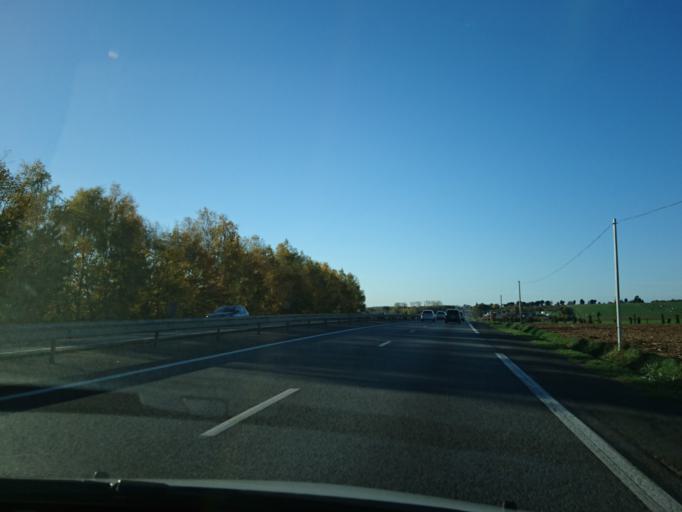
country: FR
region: Brittany
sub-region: Departement d'Ille-et-Vilaine
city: Saint-Gilles
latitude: 48.1622
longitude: -1.8568
